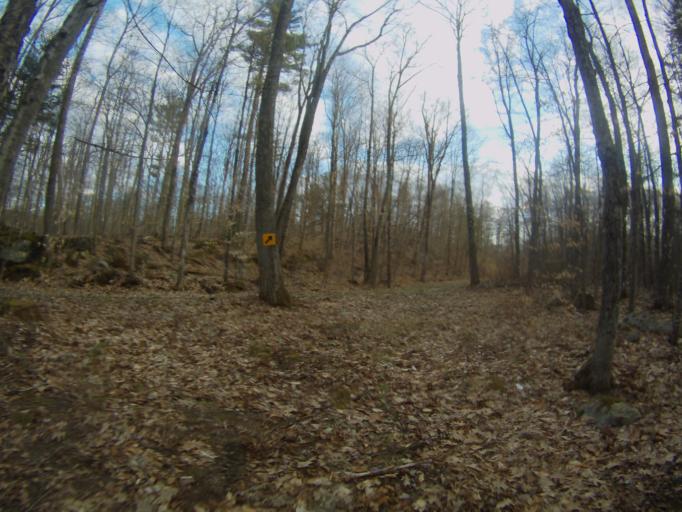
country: US
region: Vermont
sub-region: Rutland County
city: Brandon
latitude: 43.8441
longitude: -73.0352
